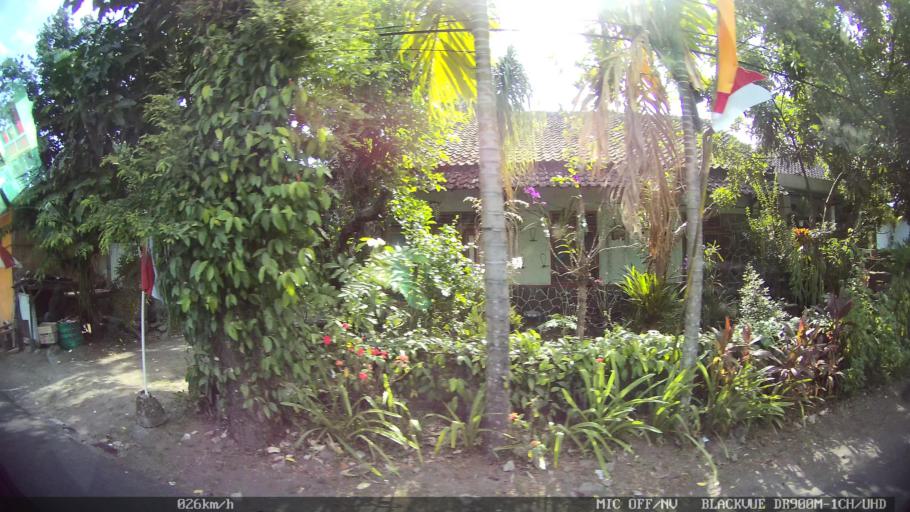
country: ID
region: Daerah Istimewa Yogyakarta
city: Gamping Lor
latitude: -7.7983
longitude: 110.3359
